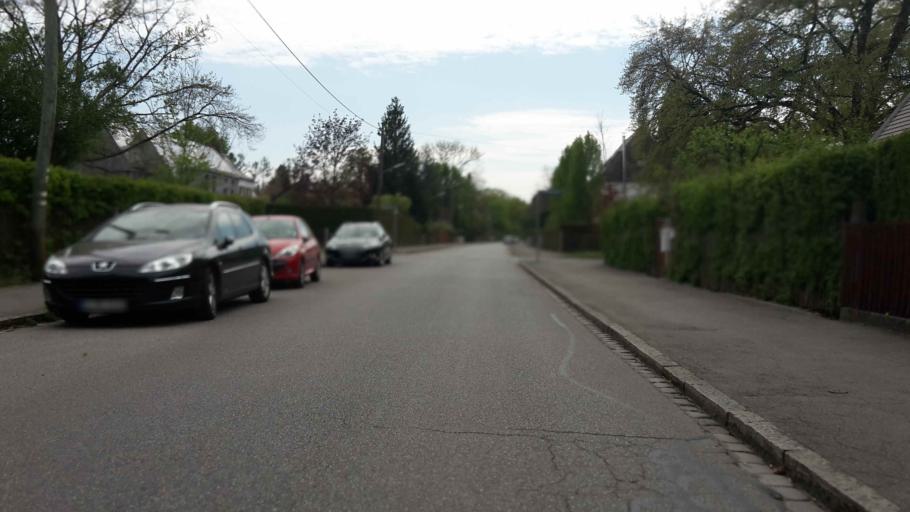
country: DE
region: Bavaria
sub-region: Upper Bavaria
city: Karlsfeld
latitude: 48.1786
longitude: 11.4893
